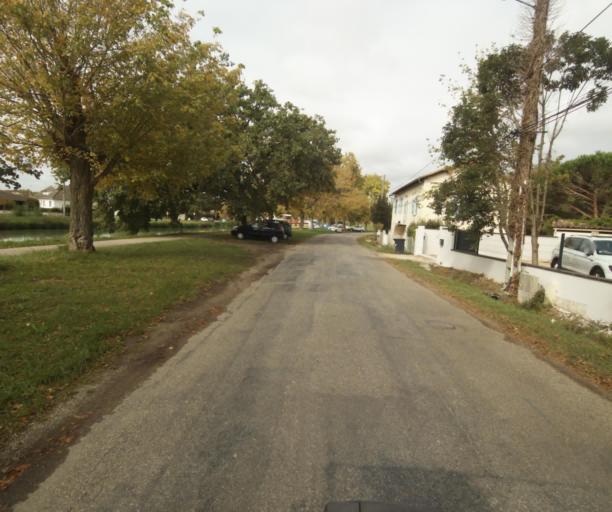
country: FR
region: Midi-Pyrenees
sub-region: Departement du Tarn-et-Garonne
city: Montech
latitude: 43.9583
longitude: 1.2392
